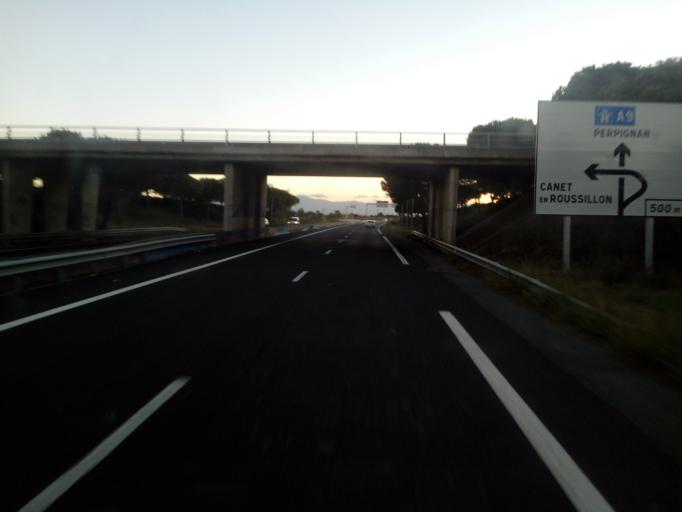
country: FR
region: Languedoc-Roussillon
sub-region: Departement des Pyrenees-Orientales
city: Le Barcares
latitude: 42.7934
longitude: 3.0251
